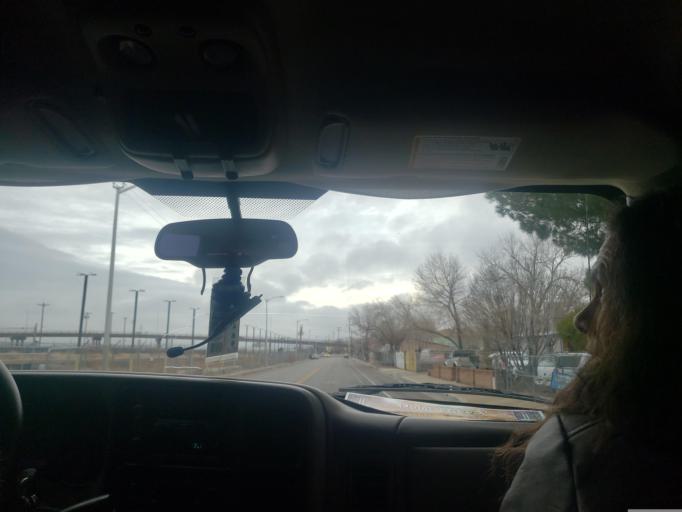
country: US
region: New Mexico
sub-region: Bernalillo County
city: Albuquerque
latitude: 35.0726
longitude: -106.6518
